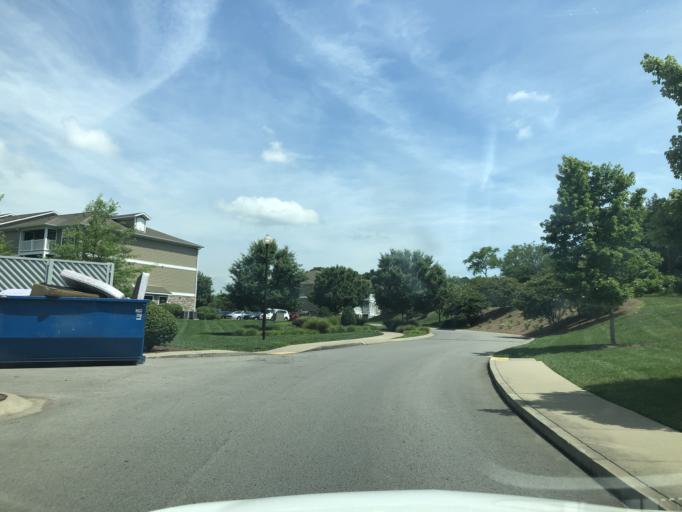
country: US
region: Tennessee
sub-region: Rutherford County
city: La Vergne
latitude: 36.0394
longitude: -86.6379
